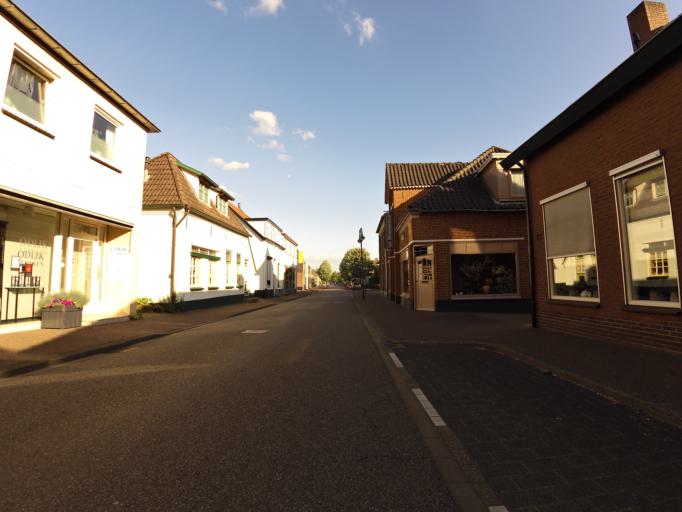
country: NL
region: Gelderland
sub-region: Oude IJsselstreek
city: Gendringen
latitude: 51.9096
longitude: 6.3815
